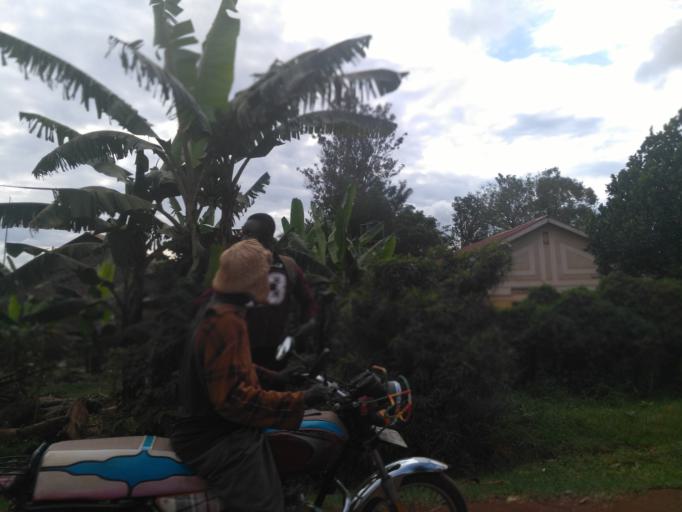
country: UG
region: Central Region
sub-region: Buikwe District
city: Njeru
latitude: 0.4184
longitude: 33.1851
